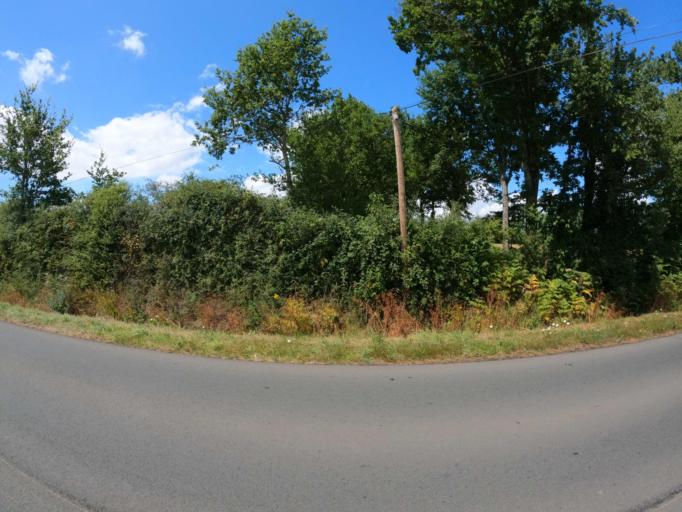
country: FR
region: Pays de la Loire
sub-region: Departement de Maine-et-Loire
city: Champigne
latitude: 47.6419
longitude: -0.5782
